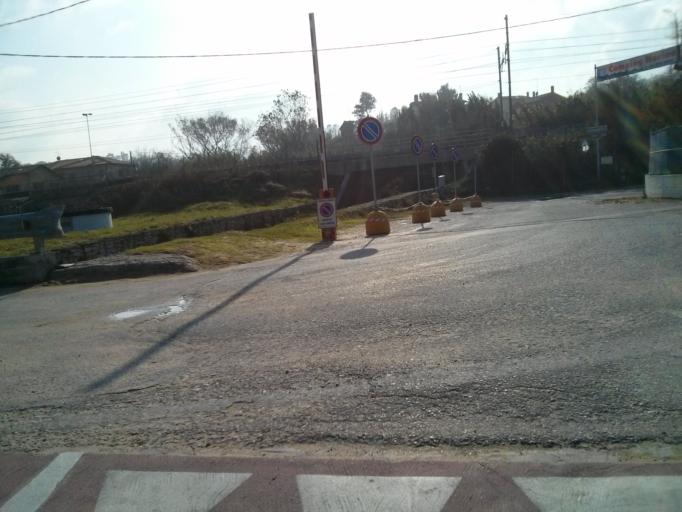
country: IT
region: The Marches
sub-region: Provincia di Pesaro e Urbino
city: Fenile
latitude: 43.8815
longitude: 12.9623
